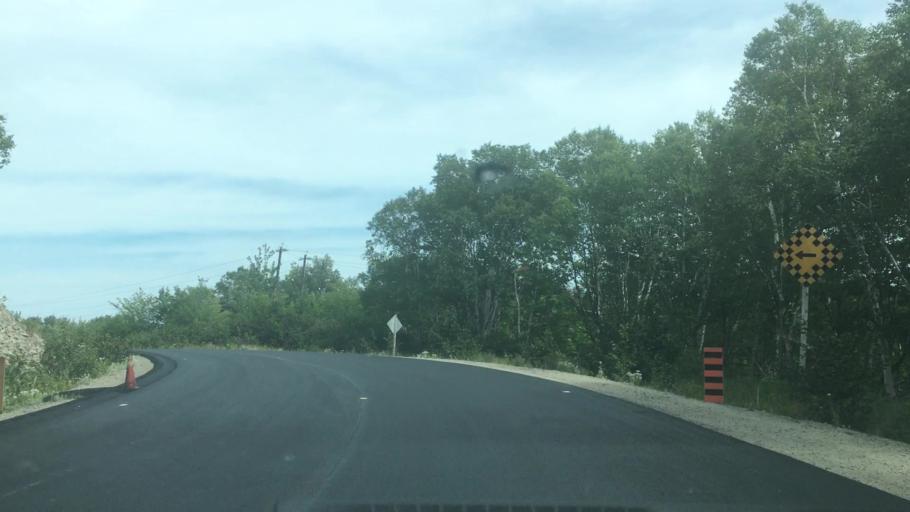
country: CA
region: Nova Scotia
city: Sydney Mines
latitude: 46.5726
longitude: -60.3933
